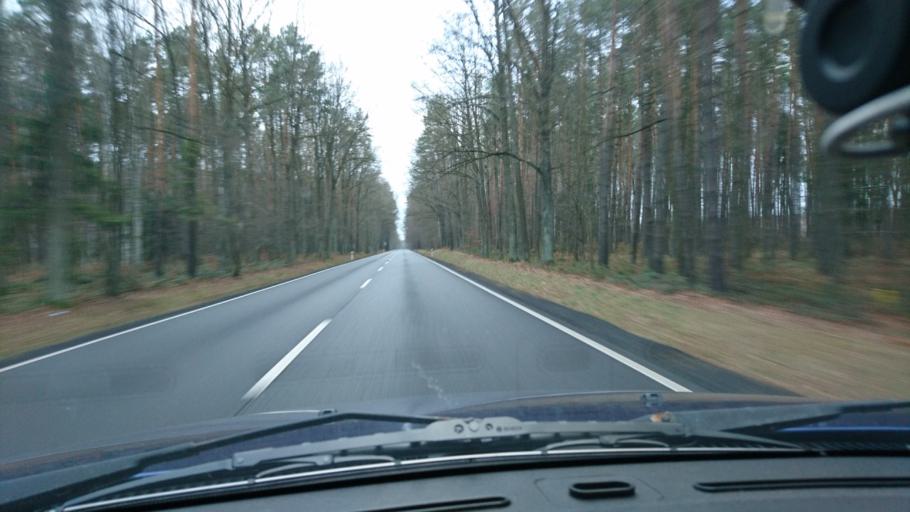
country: PL
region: Opole Voivodeship
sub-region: Powiat oleski
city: Olesno
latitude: 50.9248
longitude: 18.3371
